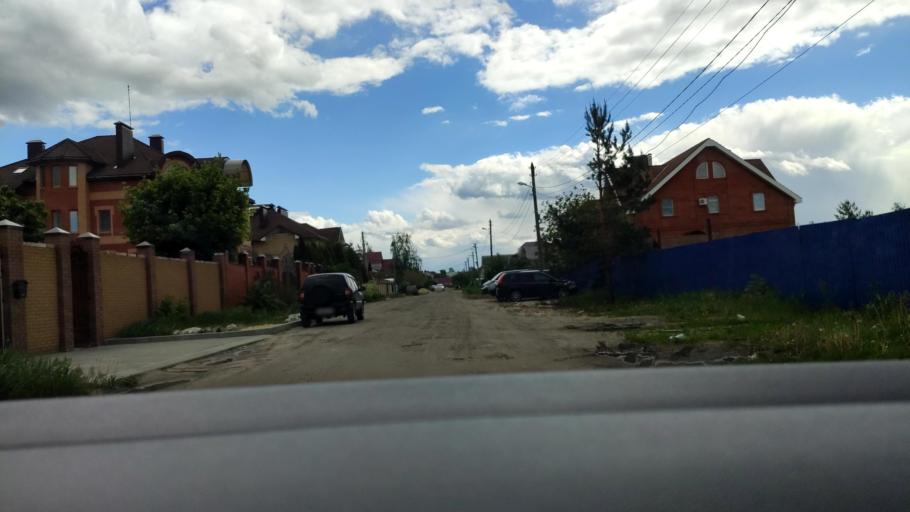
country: RU
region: Voronezj
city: Somovo
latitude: 51.6863
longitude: 39.3064
